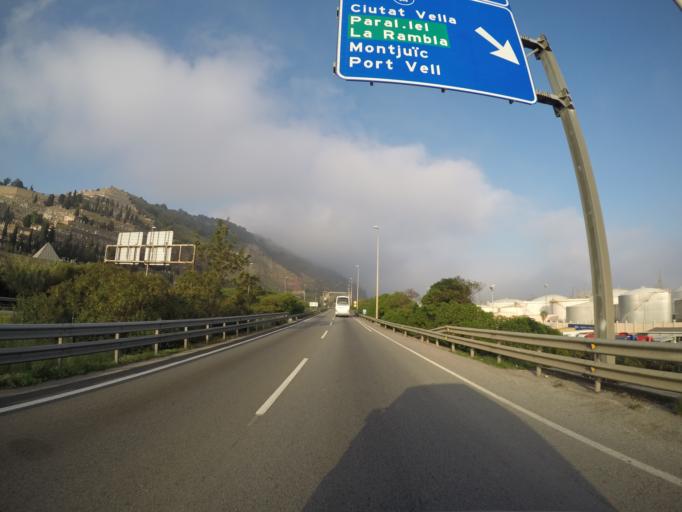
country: ES
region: Catalonia
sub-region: Provincia de Barcelona
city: Sants-Montjuic
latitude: 41.3541
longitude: 2.1591
